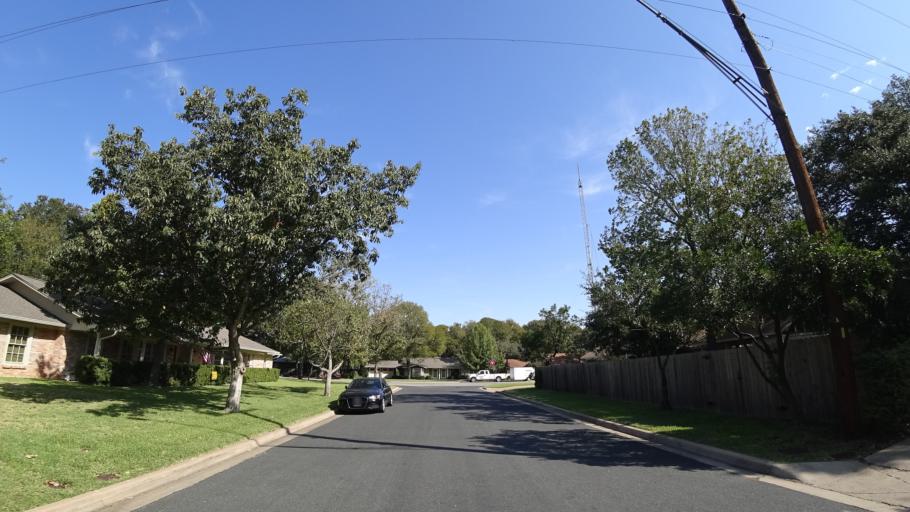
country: US
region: Texas
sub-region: Travis County
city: West Lake Hills
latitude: 30.3580
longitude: -97.7665
